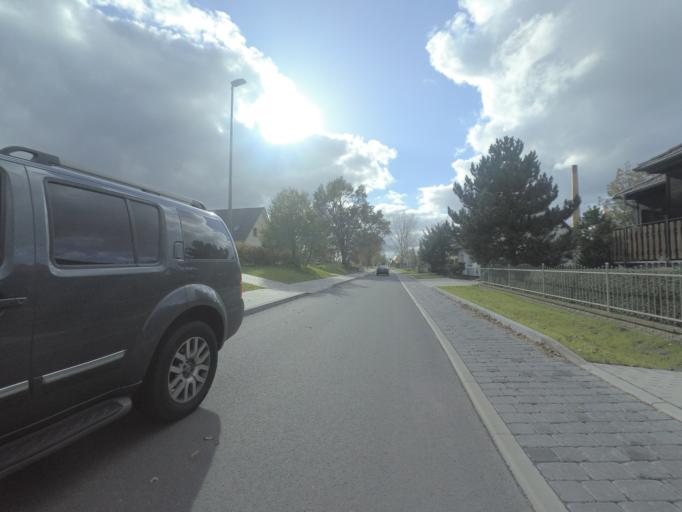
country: DE
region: Brandenburg
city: Ludwigsfelde
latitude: 52.2648
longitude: 13.3091
